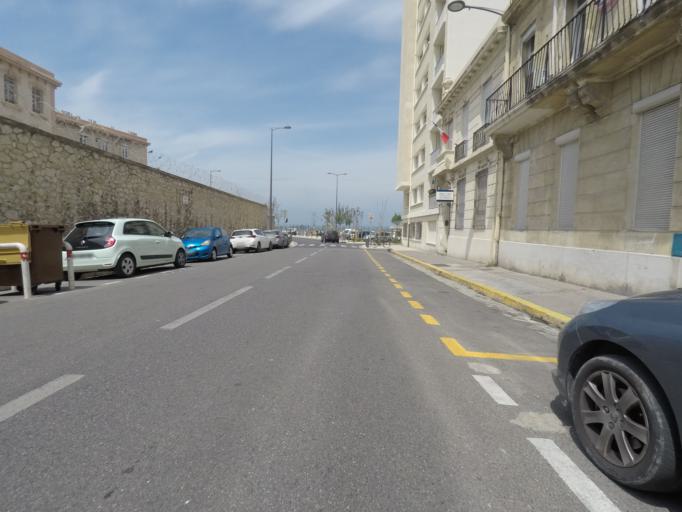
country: FR
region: Provence-Alpes-Cote d'Azur
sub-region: Departement des Bouches-du-Rhone
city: Marseille 07
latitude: 43.2898
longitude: 5.3567
